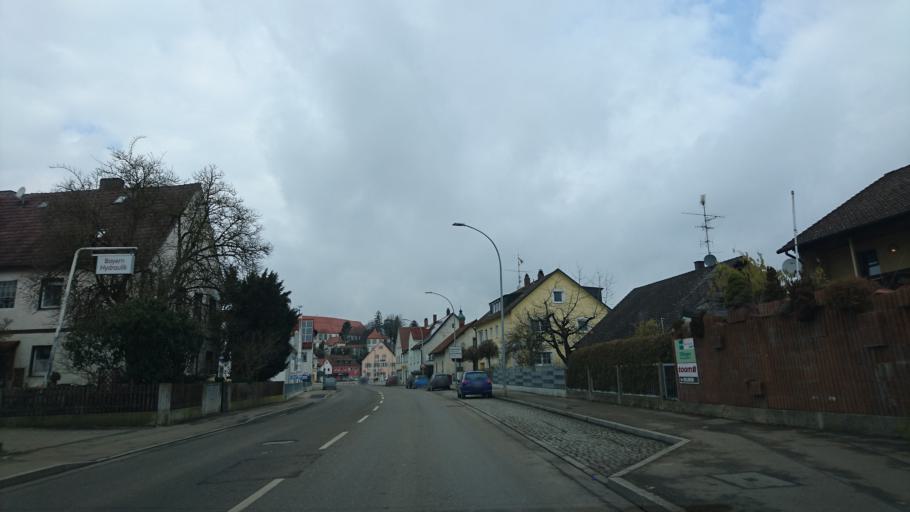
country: DE
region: Bavaria
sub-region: Swabia
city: Dillingen an der Donau
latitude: 48.5738
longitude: 10.4992
